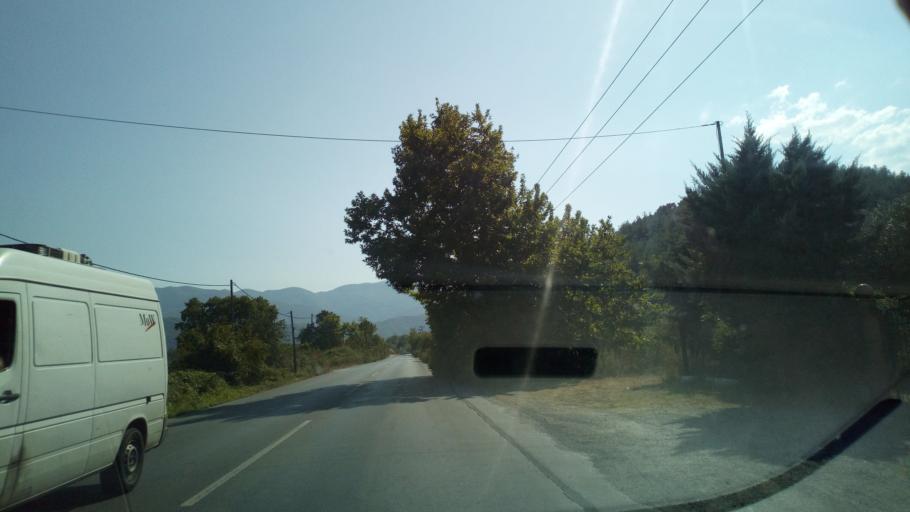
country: GR
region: Central Macedonia
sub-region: Nomos Thessalonikis
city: Stavros
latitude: 40.6098
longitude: 23.7779
